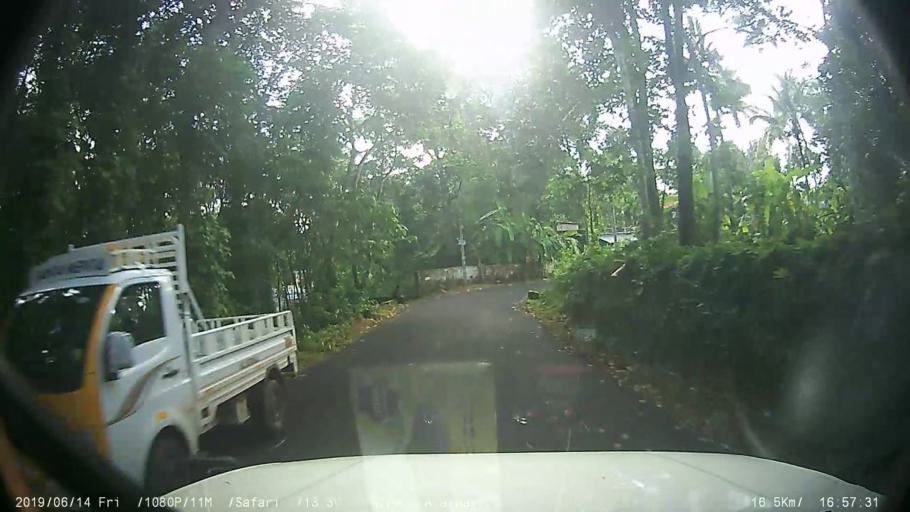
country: IN
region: Kerala
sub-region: Kottayam
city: Palackattumala
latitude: 9.7785
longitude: 76.5783
